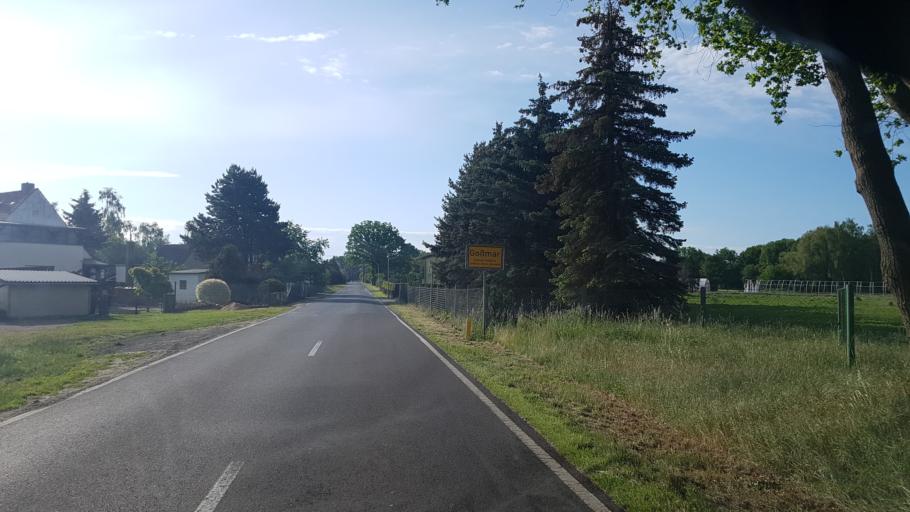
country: DE
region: Brandenburg
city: Luckau
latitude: 51.8226
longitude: 13.6884
